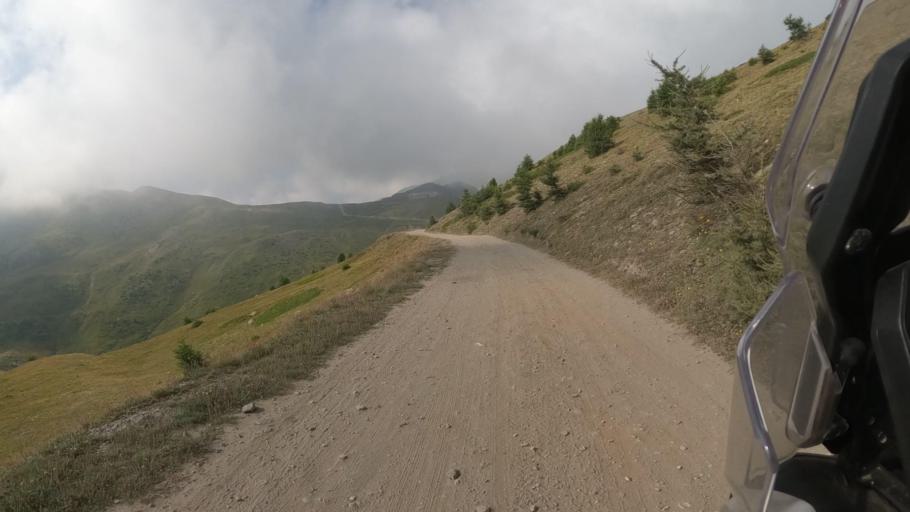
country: IT
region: Piedmont
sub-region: Provincia di Torino
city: Sestriere
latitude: 44.9917
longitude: 6.8715
